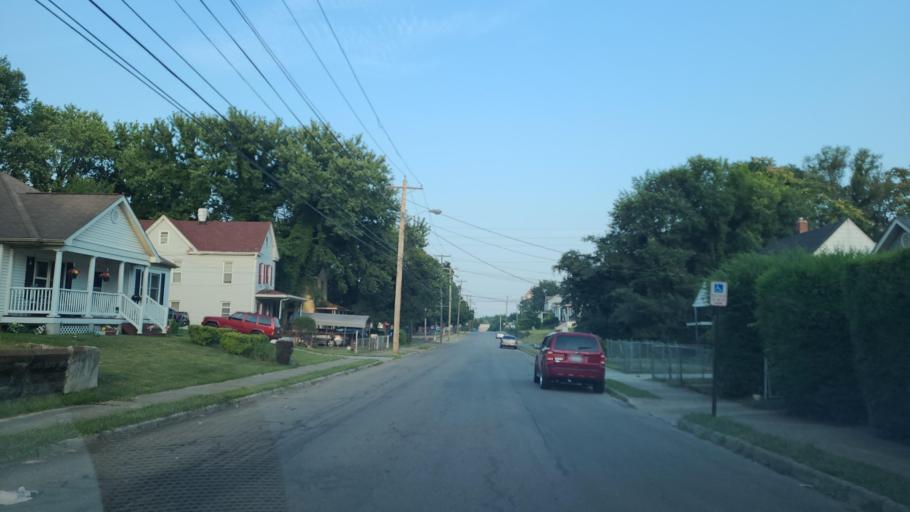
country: US
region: Virginia
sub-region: City of Roanoke
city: Roanoke
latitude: 37.2783
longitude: -79.9553
